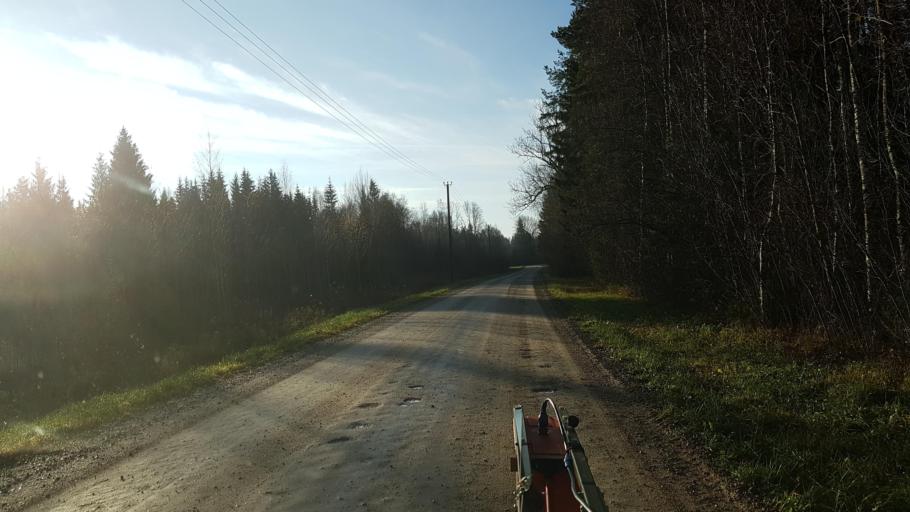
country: EE
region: Harju
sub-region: Nissi vald
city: Turba
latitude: 59.1911
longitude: 24.1396
